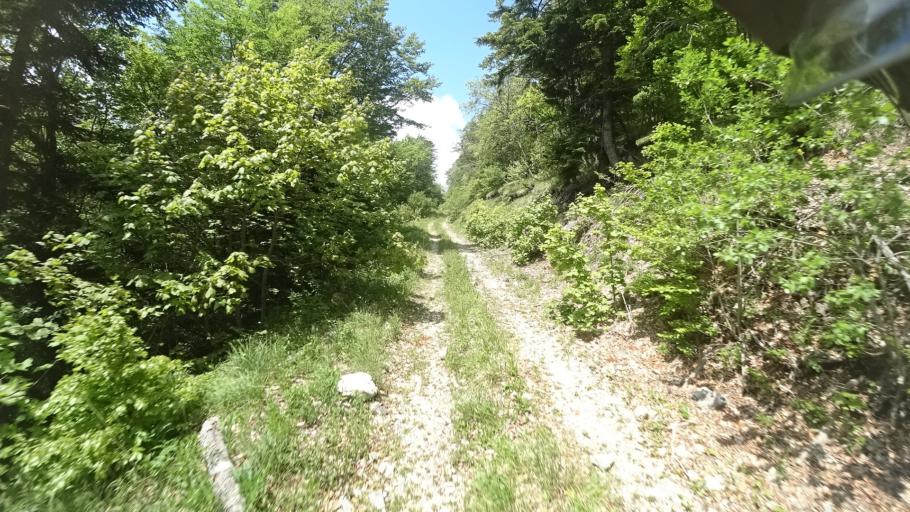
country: BA
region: Federation of Bosnia and Herzegovina
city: Orasac
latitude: 44.5662
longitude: 15.8616
